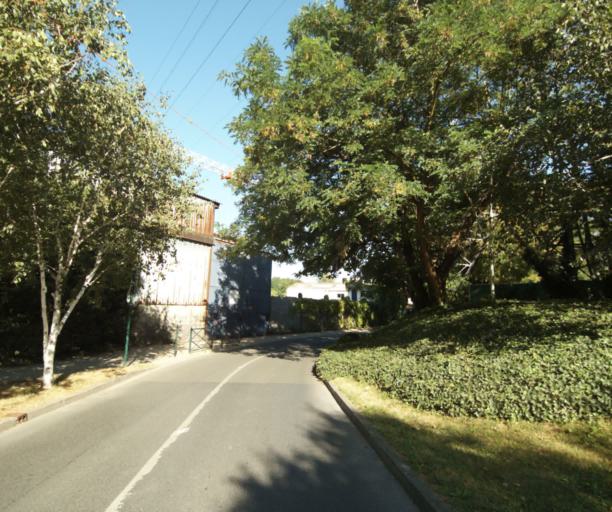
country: FR
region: Ile-de-France
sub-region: Departement des Hauts-de-Seine
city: Villeneuve-la-Garenne
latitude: 48.9432
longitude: 2.3308
